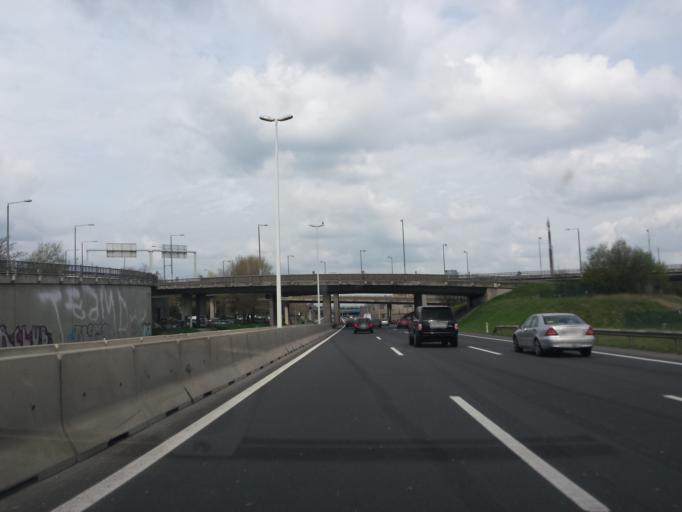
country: AT
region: Vienna
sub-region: Wien Stadt
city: Vienna
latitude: 48.2390
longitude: 16.4037
